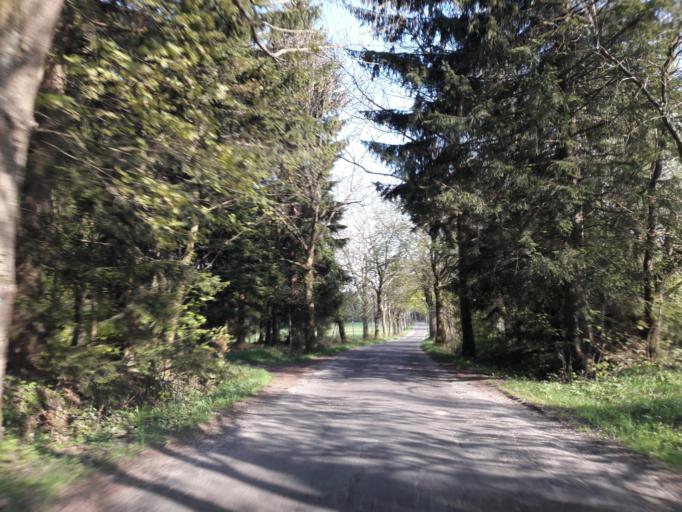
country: PL
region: Lower Silesian Voivodeship
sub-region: Powiat klodzki
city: Duszniki-Zdroj
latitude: 50.4505
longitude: 16.3447
